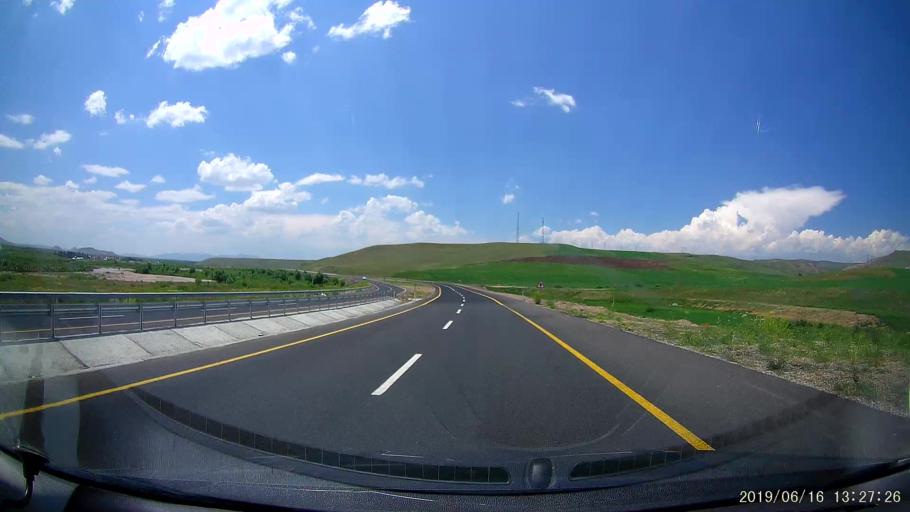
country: TR
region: Agri
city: Murat
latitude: 39.6710
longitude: 43.3105
